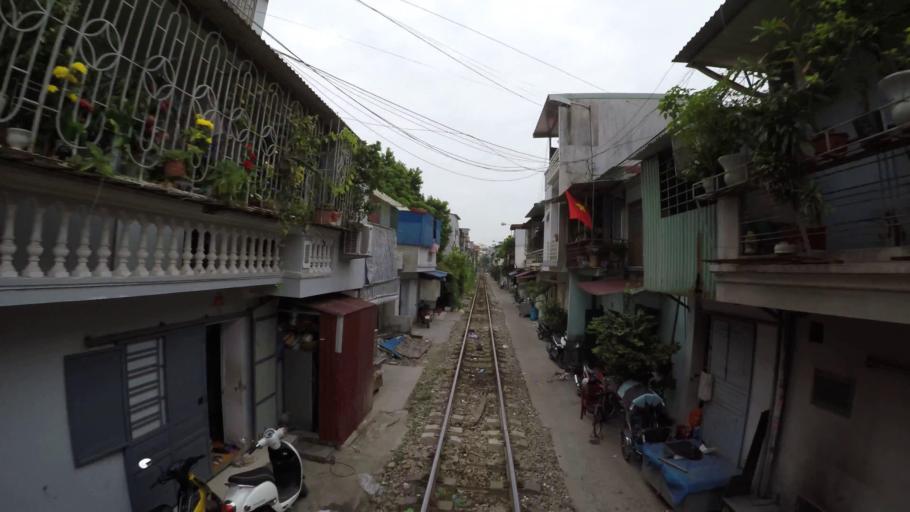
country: VN
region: Hai Phong
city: Haiphong
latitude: 20.8546
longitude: 106.6661
